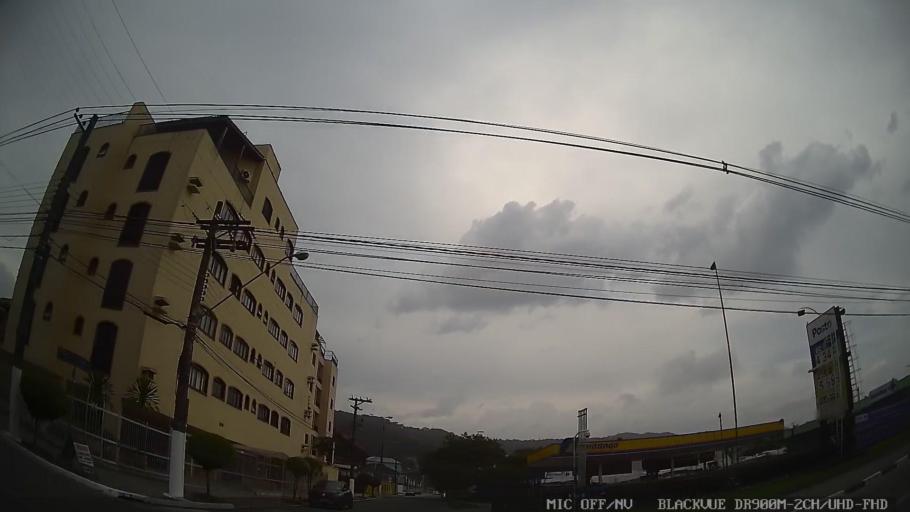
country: BR
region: Sao Paulo
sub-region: Guaruja
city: Guaruja
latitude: -23.9823
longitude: -46.2321
